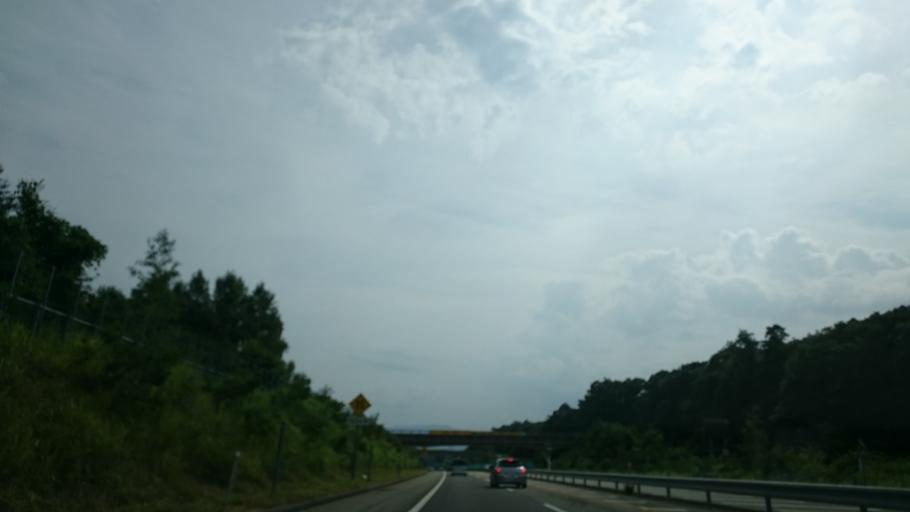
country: JP
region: Gifu
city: Gujo
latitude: 35.9834
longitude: 136.9043
